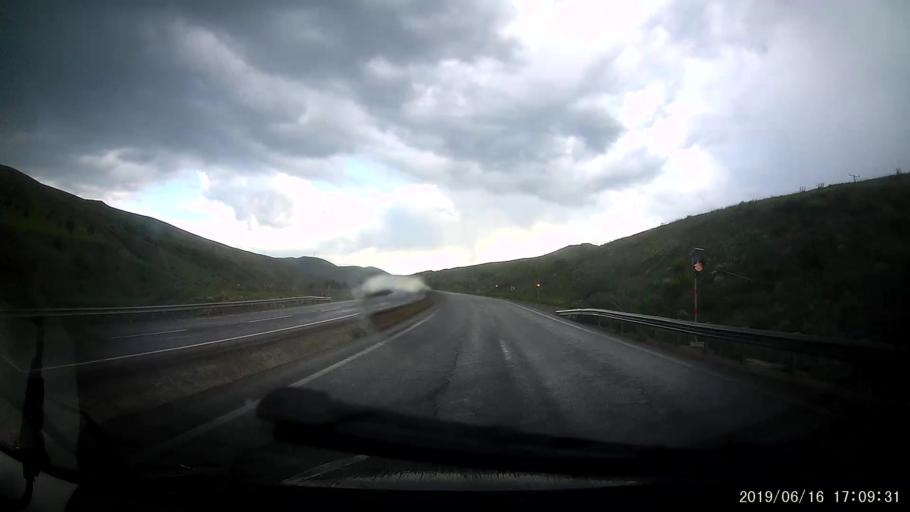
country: TR
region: Erzurum
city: Askale
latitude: 39.8939
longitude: 40.6488
